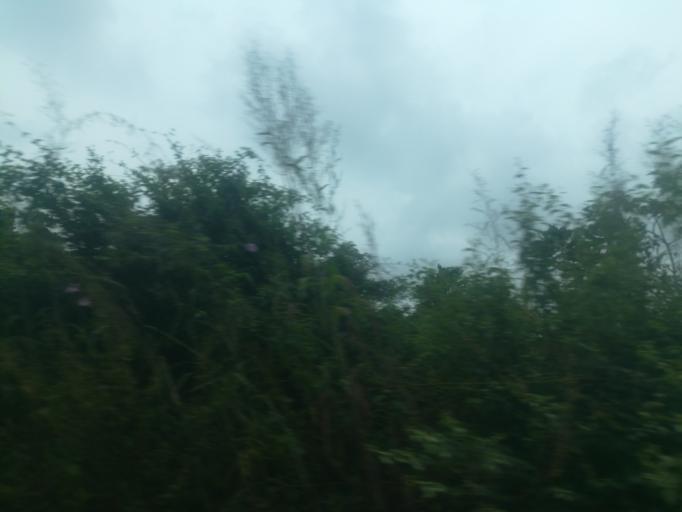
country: NG
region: Ogun
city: Ayetoro
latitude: 7.1056
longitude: 3.1420
